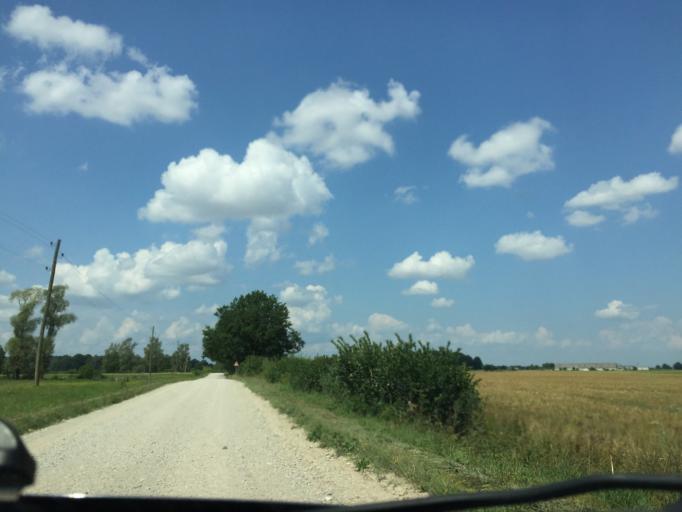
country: LT
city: Zagare
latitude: 56.3875
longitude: 23.2655
